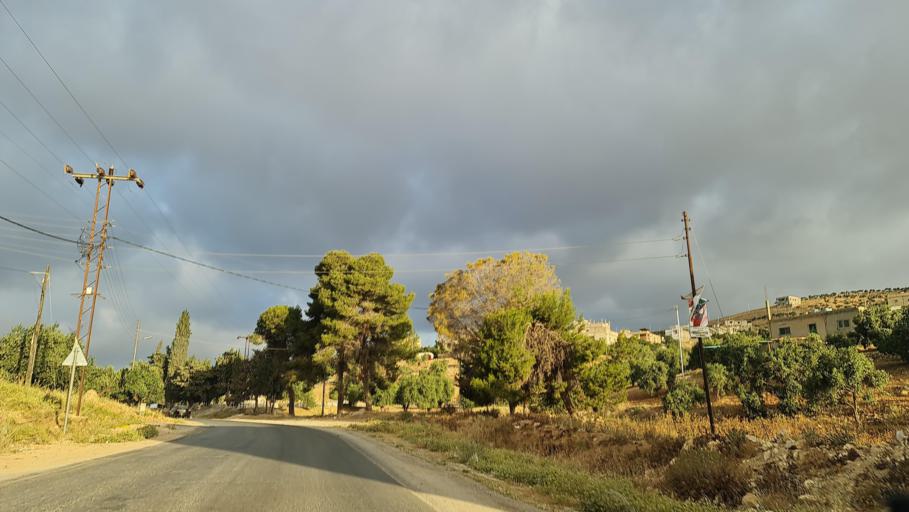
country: JO
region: Amman
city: Al Jubayhah
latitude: 32.0931
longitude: 35.9248
